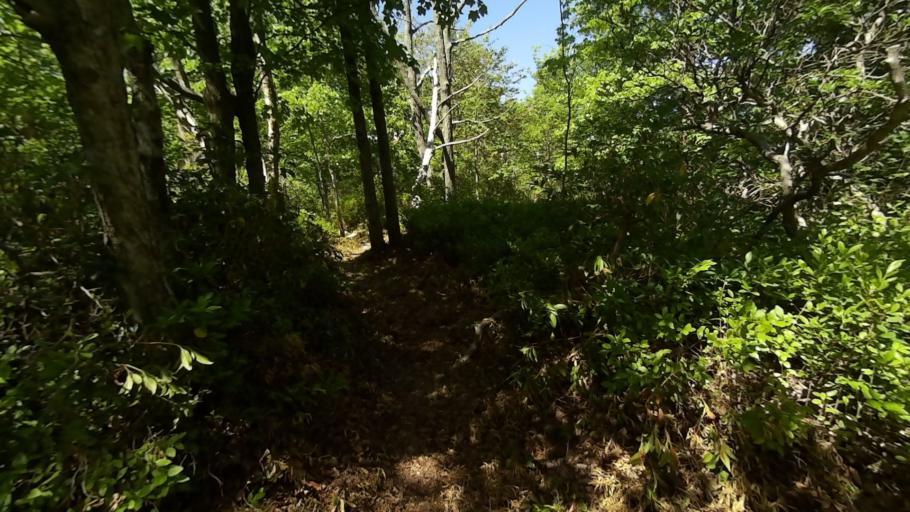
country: US
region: Pennsylvania
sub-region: Centre County
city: Boalsburg
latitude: 40.7195
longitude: -77.7824
